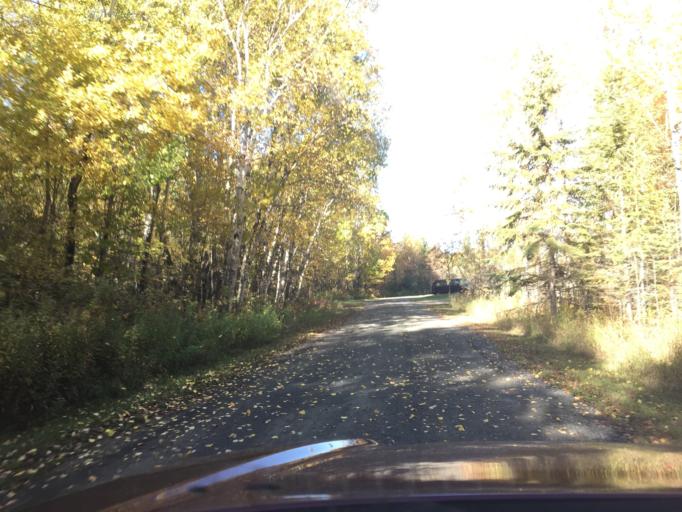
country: US
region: Minnesota
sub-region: Lake of the Woods County
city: Baudette
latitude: 48.2853
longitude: -94.5646
